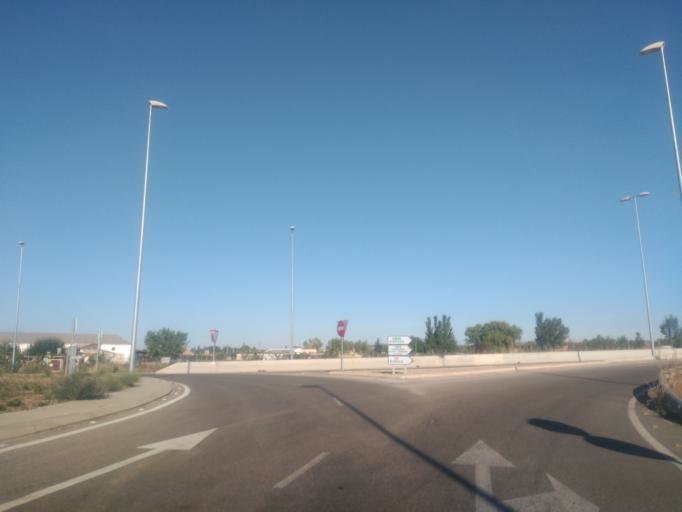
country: ES
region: Castille and Leon
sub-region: Provincia de Burgos
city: Aranda de Duero
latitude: 41.6761
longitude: -3.6589
